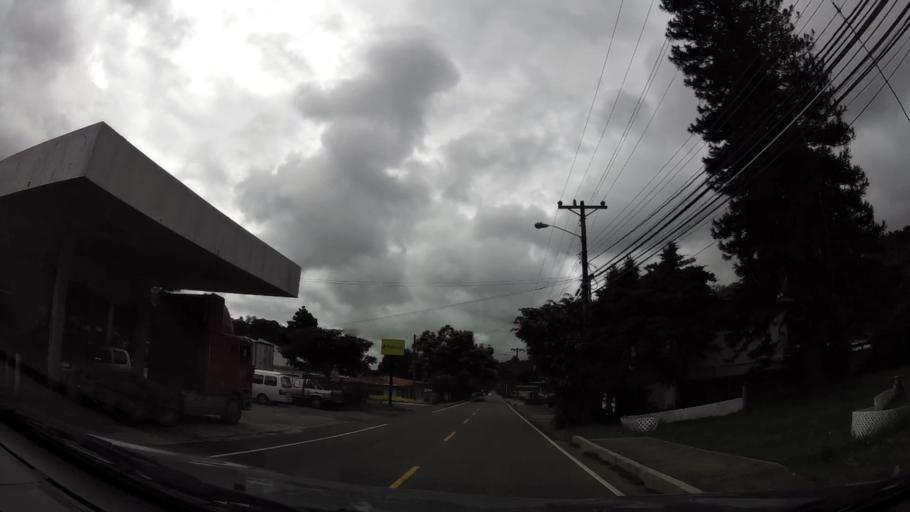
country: PA
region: Chiriqui
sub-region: Distrito Boquete
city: Boquete
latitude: 8.7724
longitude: -82.4329
